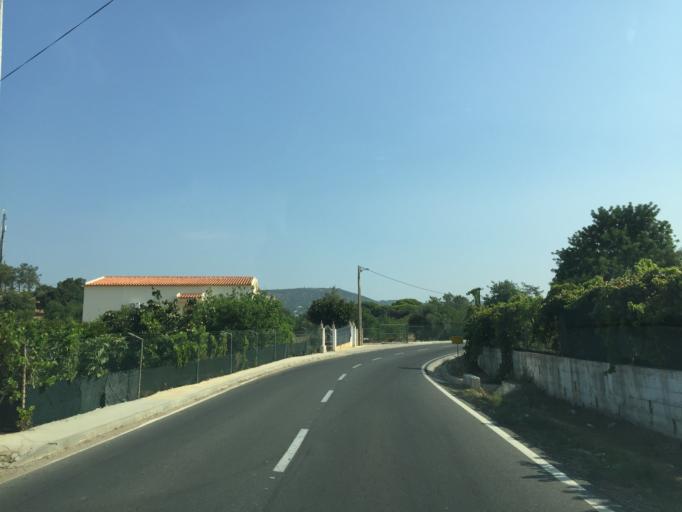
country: PT
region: Faro
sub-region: Loule
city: Almancil
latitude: 37.0838
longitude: -7.9950
